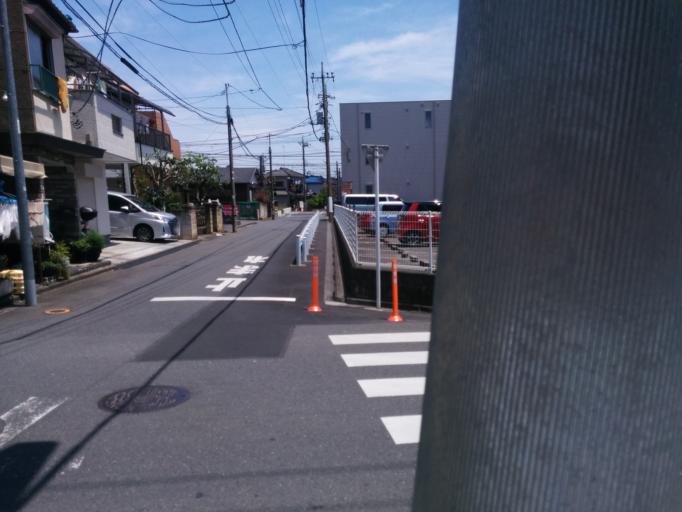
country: JP
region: Tokyo
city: Higashimurayama-shi
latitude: 35.7649
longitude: 139.4664
